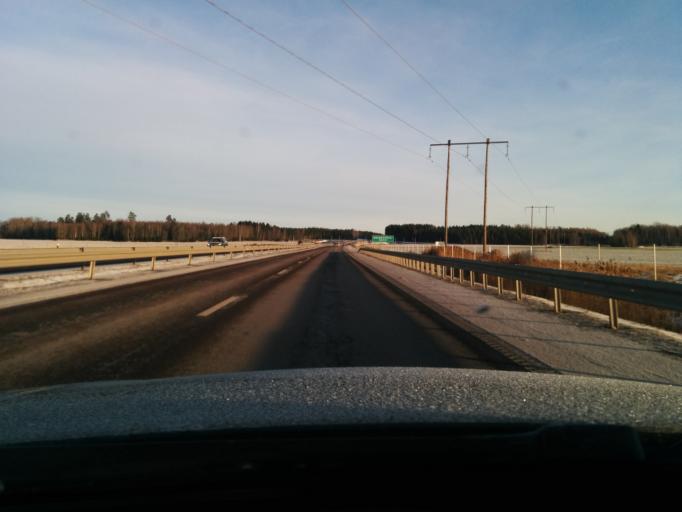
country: SE
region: Vaestmanland
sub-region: Vasteras
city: Tillberga
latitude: 59.6168
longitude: 16.6500
